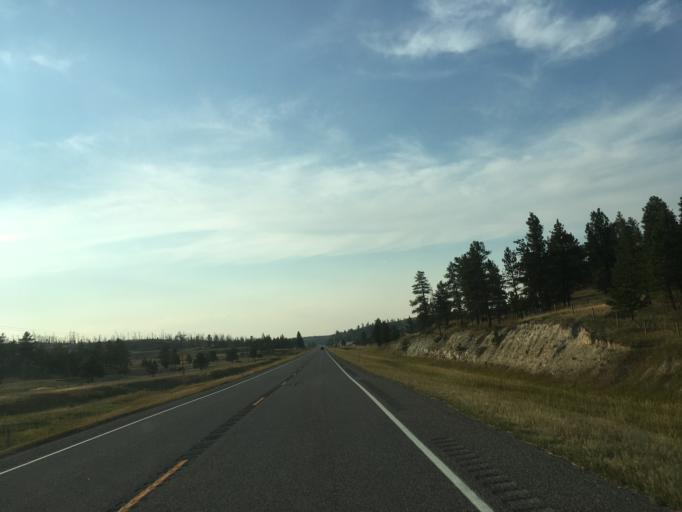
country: US
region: Montana
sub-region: Musselshell County
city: Roundup
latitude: 46.2837
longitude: -108.4784
